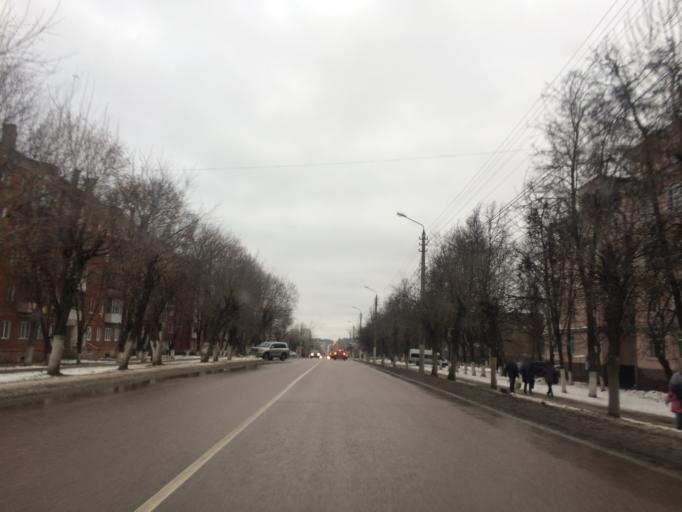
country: RU
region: Tula
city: Tula
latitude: 54.2111
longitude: 37.6684
